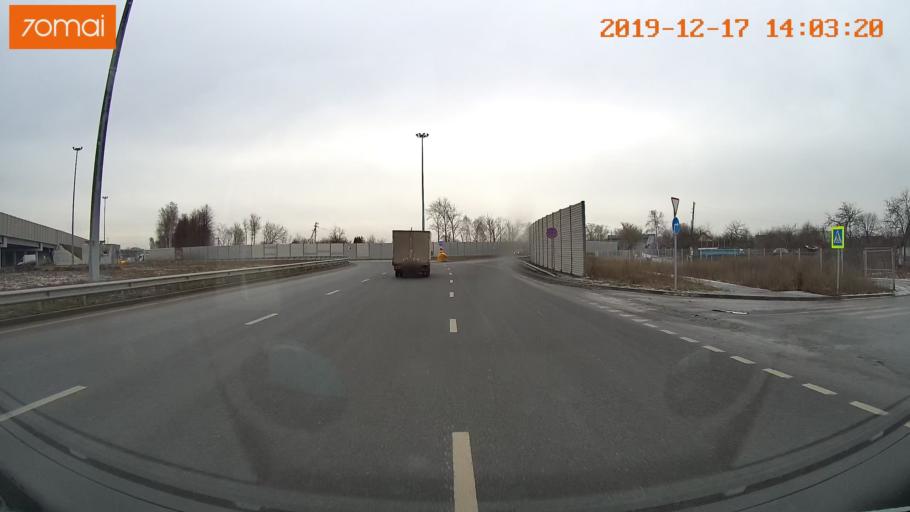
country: RU
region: Rjazan
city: Ryazan'
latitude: 54.6101
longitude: 39.6393
